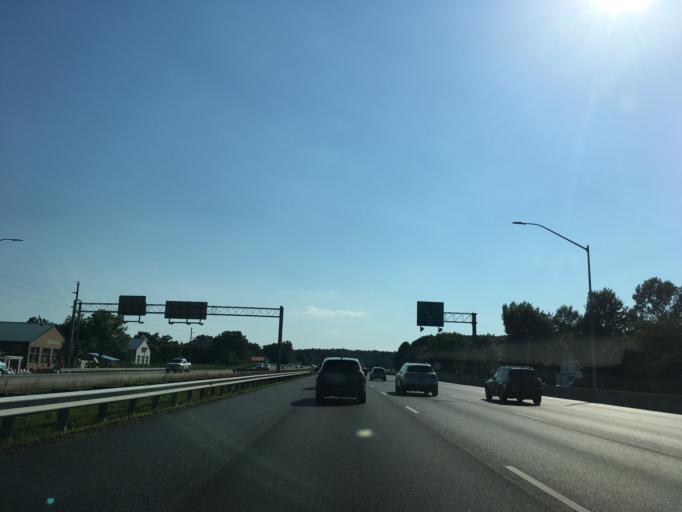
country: US
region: Maryland
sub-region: Queen Anne's County
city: Grasonville
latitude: 38.9634
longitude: -76.1983
